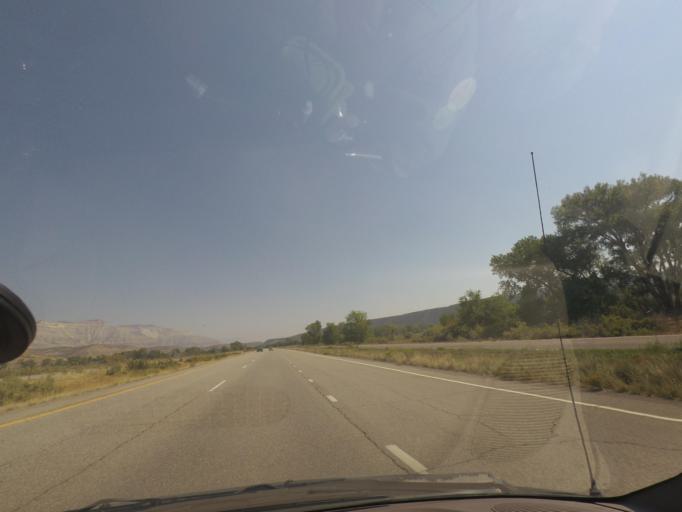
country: US
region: Colorado
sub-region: Garfield County
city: Parachute
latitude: 39.3281
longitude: -108.2017
